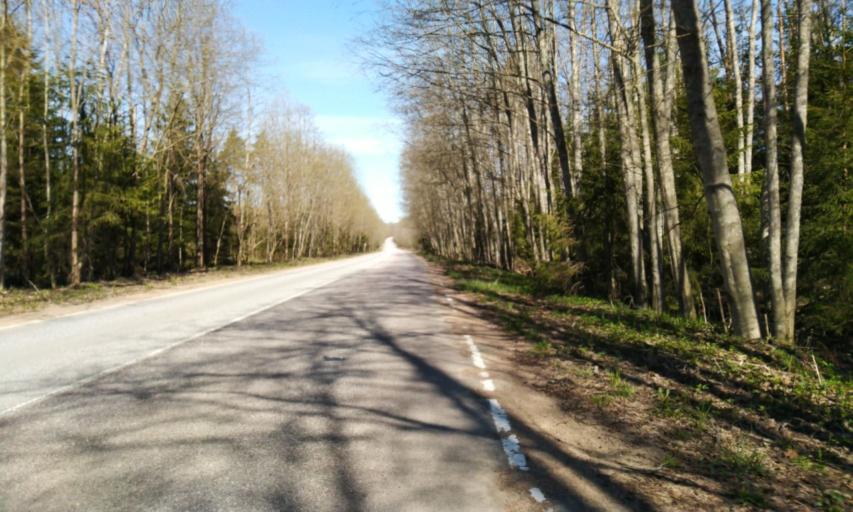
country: RU
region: Leningrad
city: Garbolovo
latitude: 60.4032
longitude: 30.4726
